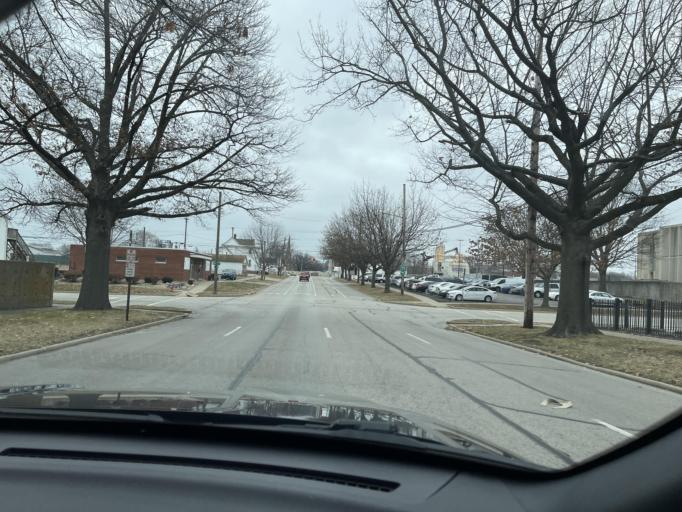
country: US
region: Illinois
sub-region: Sangamon County
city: Springfield
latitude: 39.7938
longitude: -89.6457
